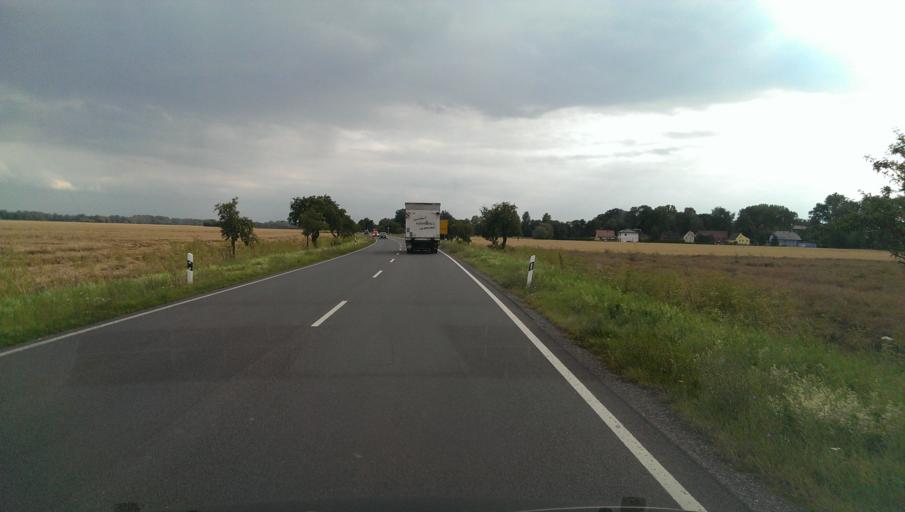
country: DE
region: Saxony
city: Pegau
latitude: 51.1558
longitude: 12.2491
